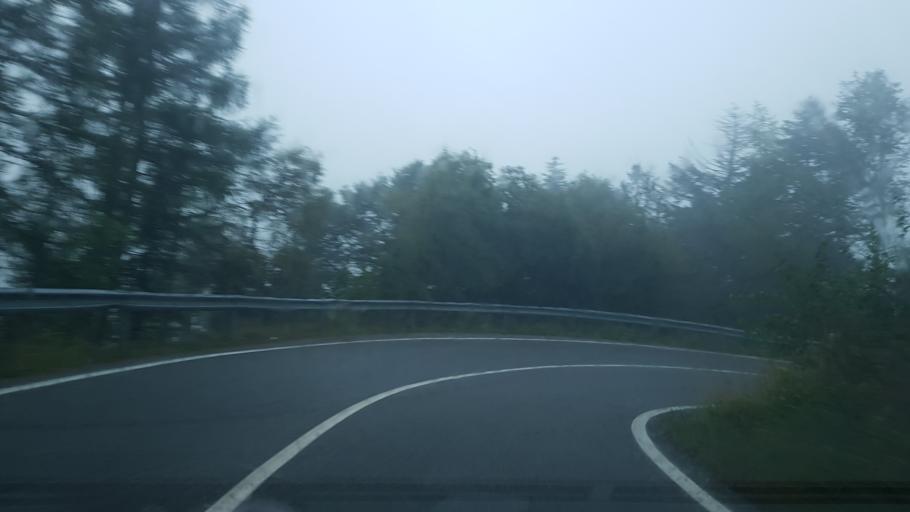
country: IT
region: Piedmont
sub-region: Provincia di Cuneo
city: Frabosa Soprana
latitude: 44.2585
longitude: 7.7724
